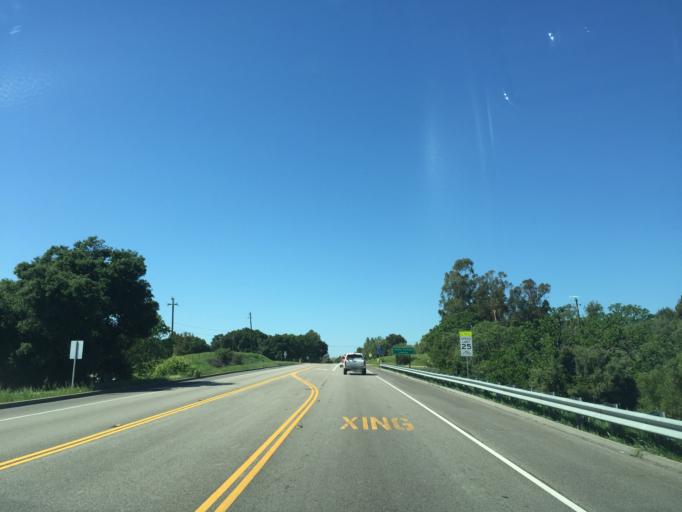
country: US
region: California
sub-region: Santa Barbara County
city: Los Olivos
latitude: 34.6645
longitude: -120.1088
